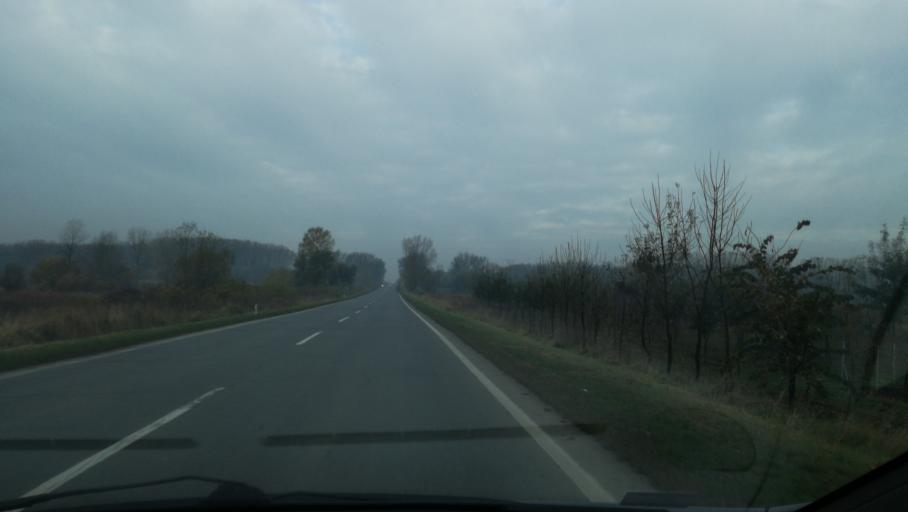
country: RS
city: Aradac
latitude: 45.3926
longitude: 20.2237
